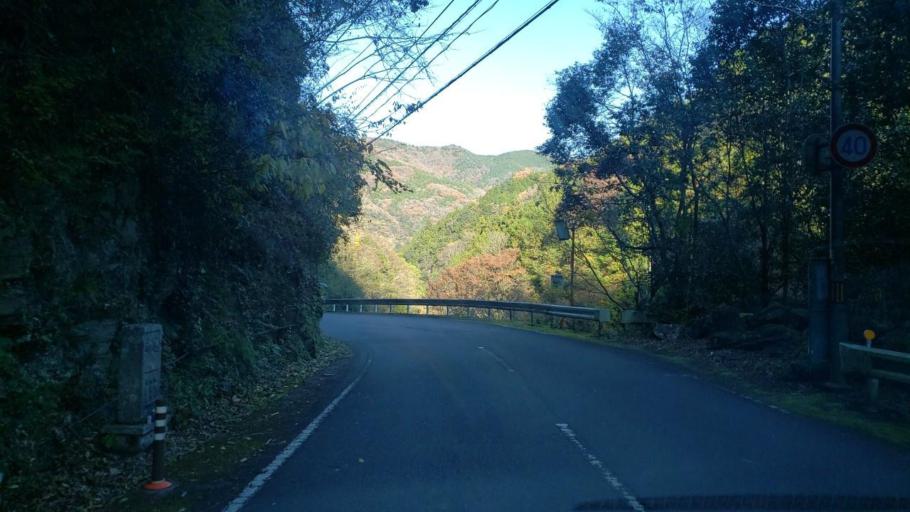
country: JP
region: Tokushima
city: Wakimachi
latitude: 34.0138
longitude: 134.0316
